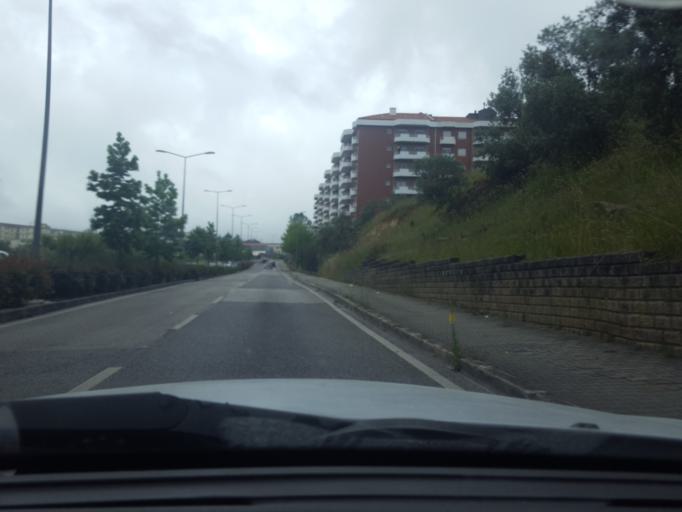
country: PT
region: Leiria
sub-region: Leiria
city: Leiria
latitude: 39.7345
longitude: -8.8034
